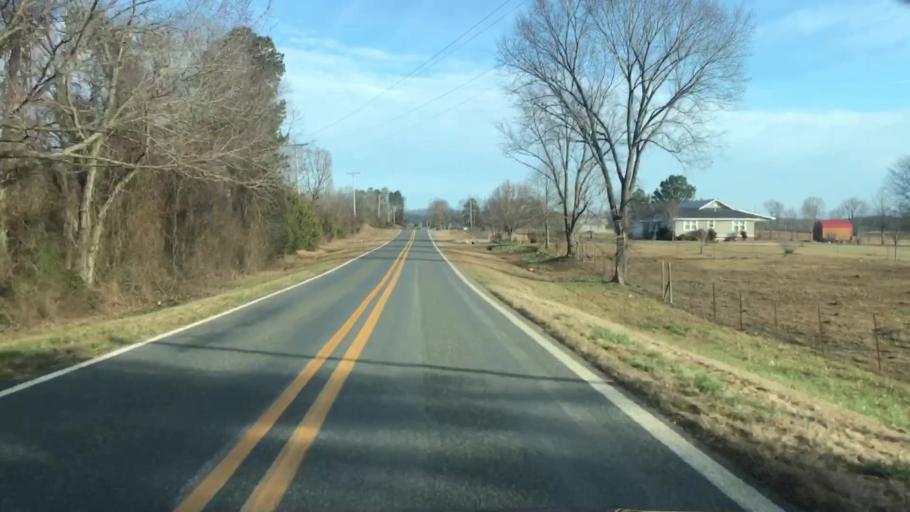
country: US
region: Arkansas
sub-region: Garland County
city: Rockwell
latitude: 34.4982
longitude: -93.2765
